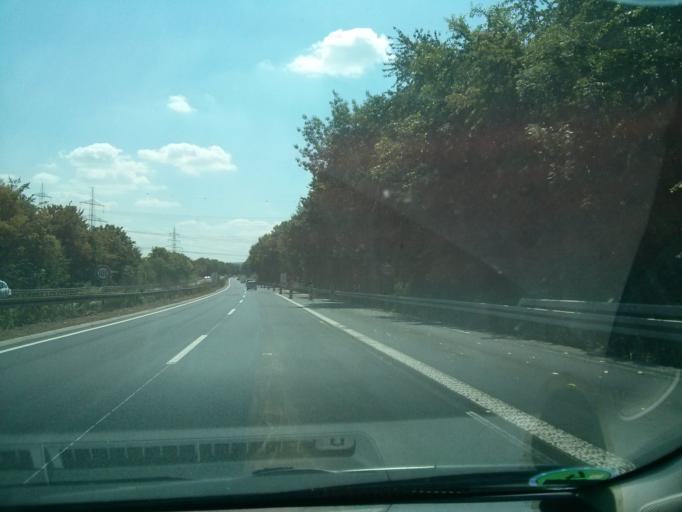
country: DE
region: North Rhine-Westphalia
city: Meckenheim
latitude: 50.6115
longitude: 7.0418
